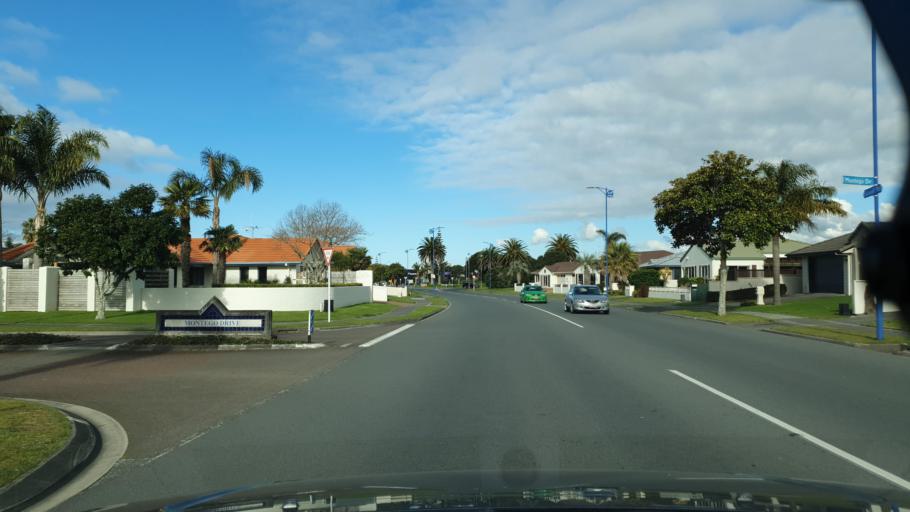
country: NZ
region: Bay of Plenty
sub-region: Tauranga City
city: Tauranga
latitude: -37.7000
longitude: 176.2766
